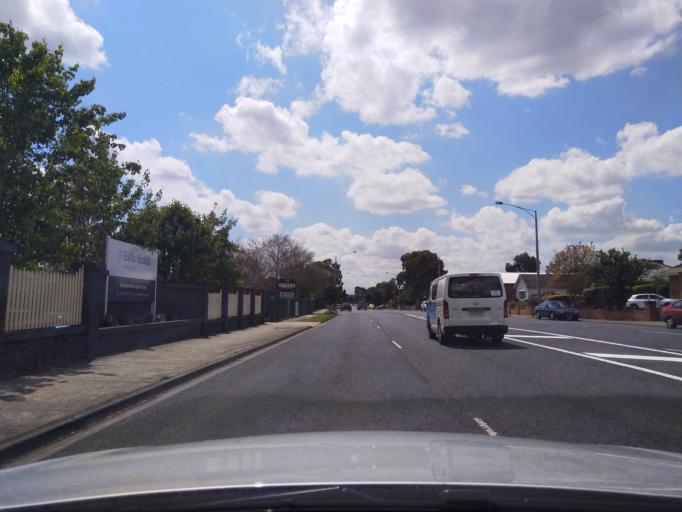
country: AU
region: Victoria
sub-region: Banyule
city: Bellfield
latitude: -37.7482
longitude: 145.0466
